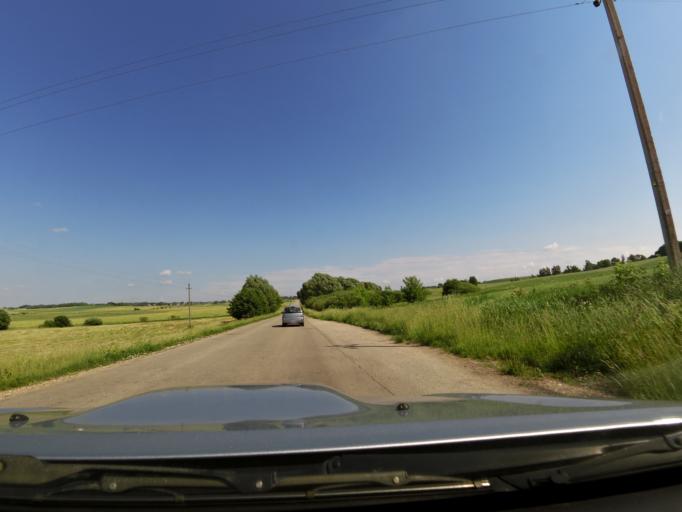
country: LT
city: Vilkaviskis
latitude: 54.5076
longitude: 22.9958
